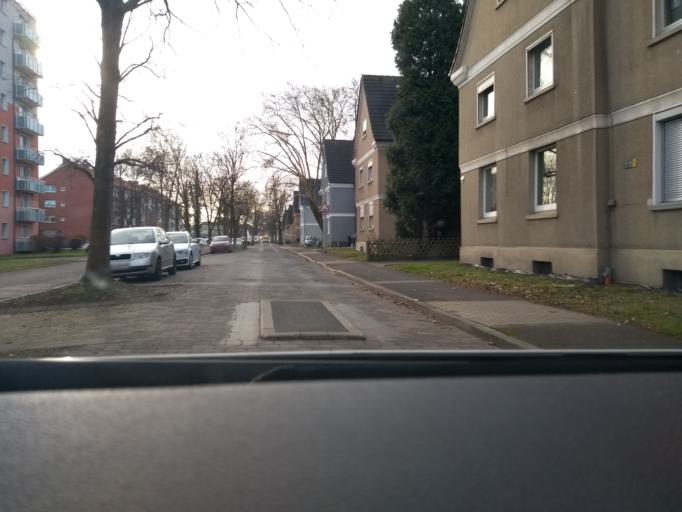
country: DE
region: North Rhine-Westphalia
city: Waltrop
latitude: 51.6014
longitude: 7.4489
